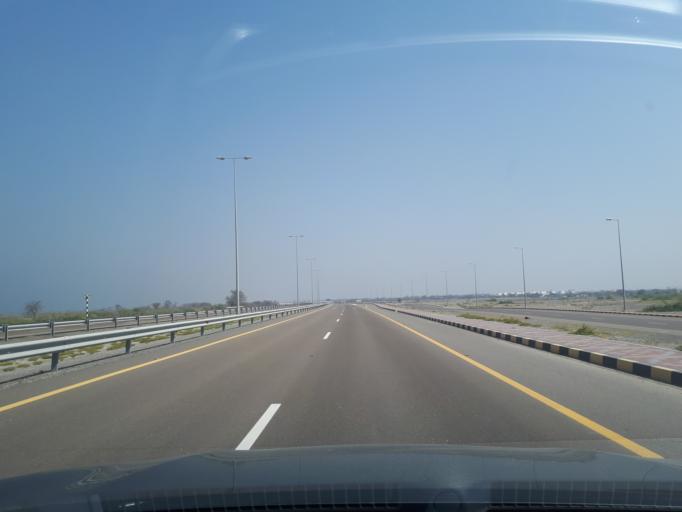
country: AE
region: Al Fujayrah
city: Al Fujayrah
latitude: 24.9275
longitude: 56.3845
